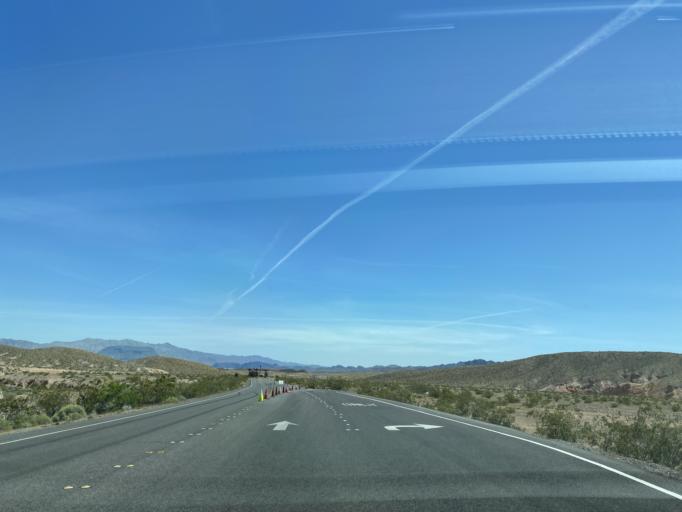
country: US
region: Nevada
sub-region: Clark County
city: Henderson
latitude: 36.1633
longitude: -114.9080
